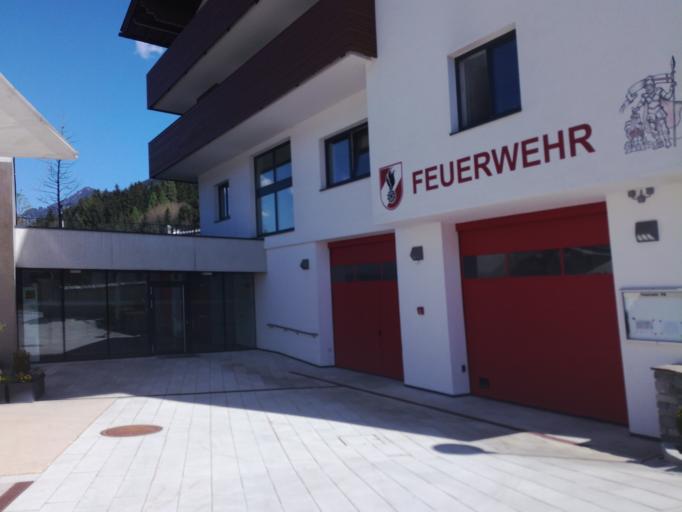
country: AT
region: Tyrol
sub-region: Politischer Bezirk Schwaz
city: Pill
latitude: 47.3207
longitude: 11.6816
